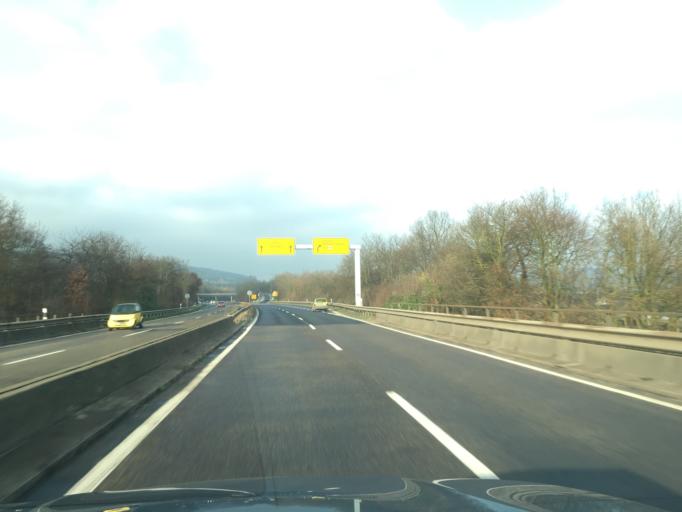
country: DE
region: Rheinland-Pfalz
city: Sinzig
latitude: 50.5521
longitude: 7.2537
